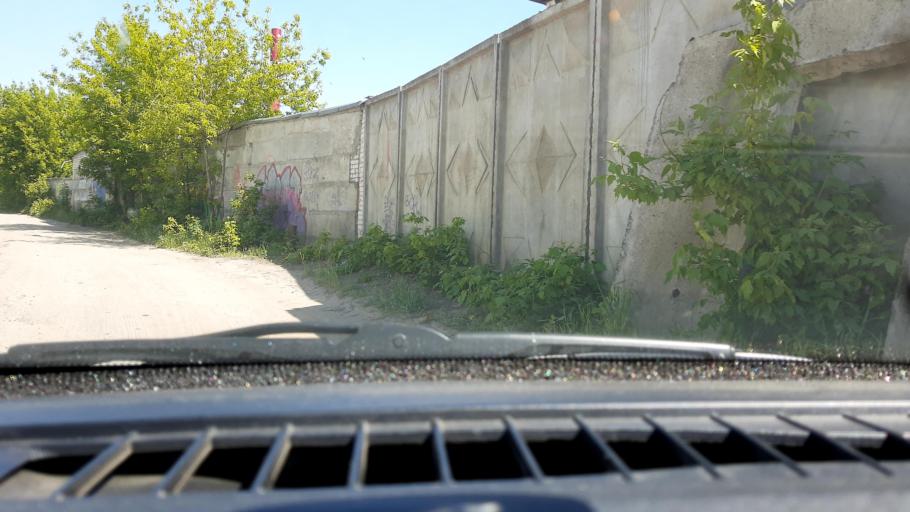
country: RU
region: Nizjnij Novgorod
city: Neklyudovo
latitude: 56.3559
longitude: 43.8485
